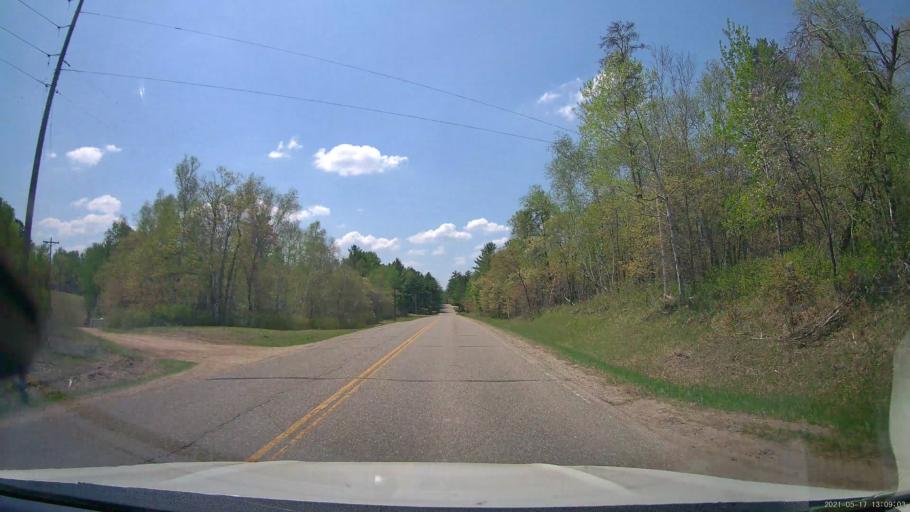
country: US
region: Minnesota
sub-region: Hubbard County
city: Park Rapids
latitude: 47.0309
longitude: -94.9240
